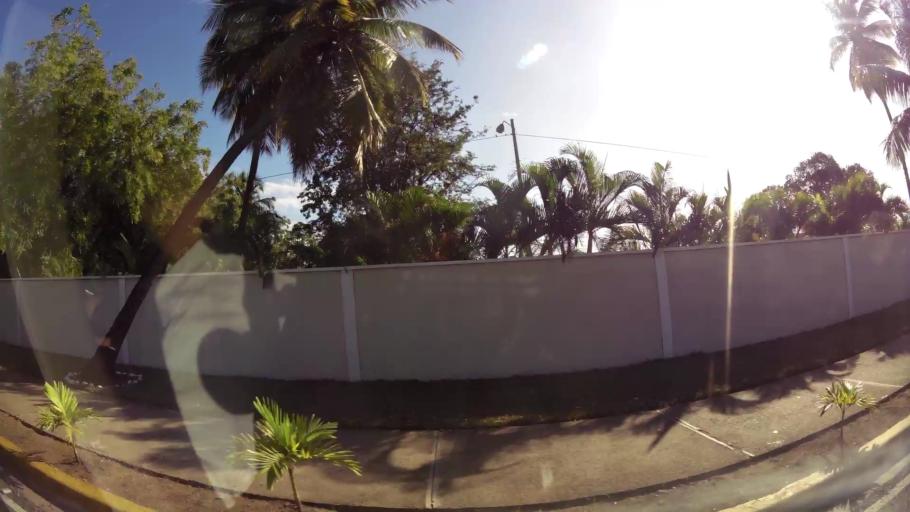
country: DO
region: Nacional
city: Ciudad Nueva
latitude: 18.4729
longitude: -69.8762
